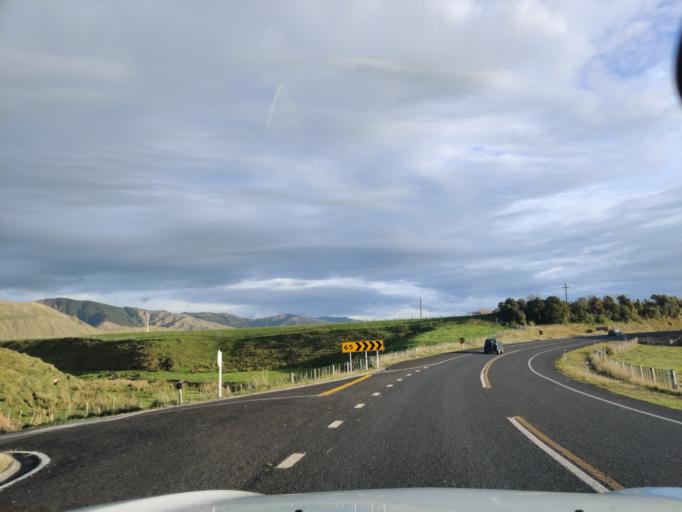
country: NZ
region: Manawatu-Wanganui
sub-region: Horowhenua District
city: Foxton
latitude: -40.5075
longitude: 175.4850
